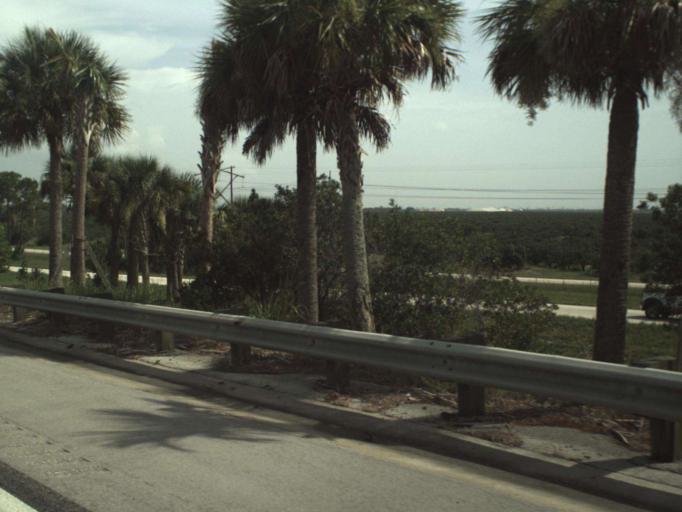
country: US
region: Florida
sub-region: Saint Lucie County
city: Lakewood Park
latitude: 27.5199
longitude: -80.4501
